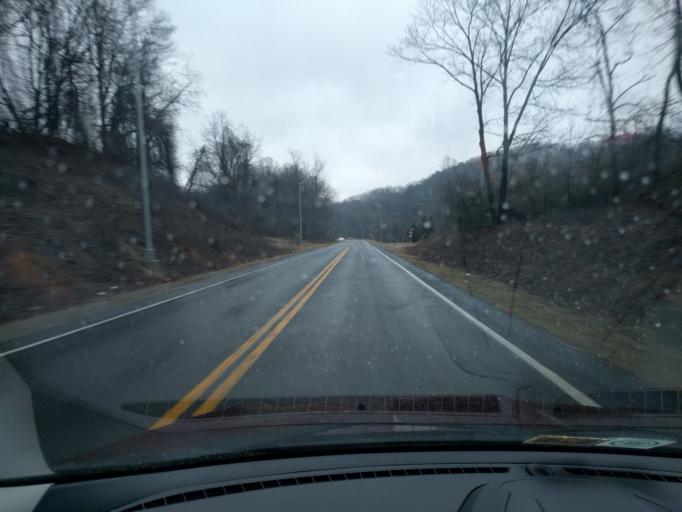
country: US
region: Virginia
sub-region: Pulaski County
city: Pulaski
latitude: 37.0377
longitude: -80.7366
